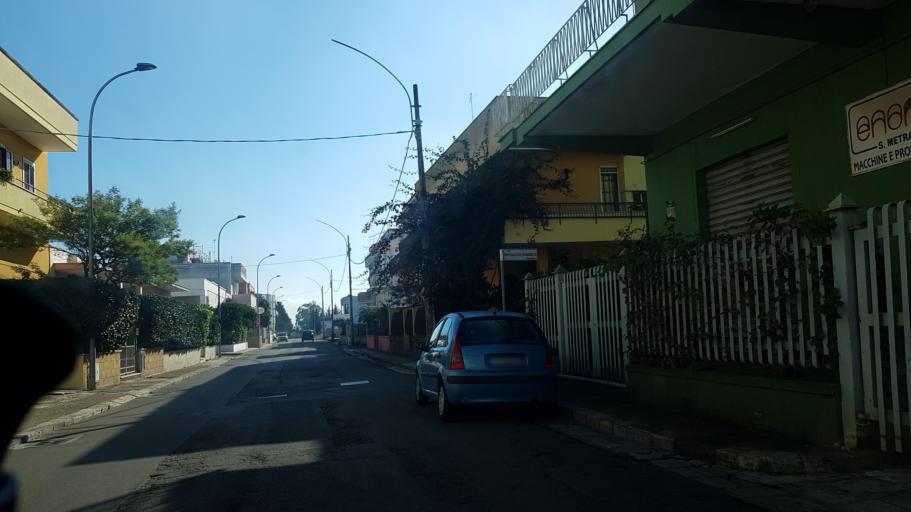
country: IT
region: Apulia
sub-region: Provincia di Lecce
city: Novoli
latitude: 40.3744
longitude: 18.0521
